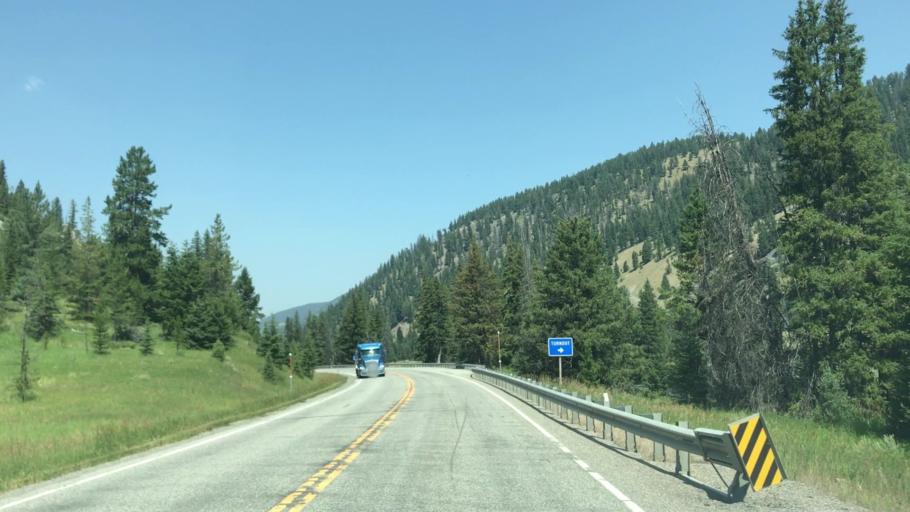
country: US
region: Montana
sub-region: Gallatin County
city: Big Sky
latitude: 45.0821
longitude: -111.2085
